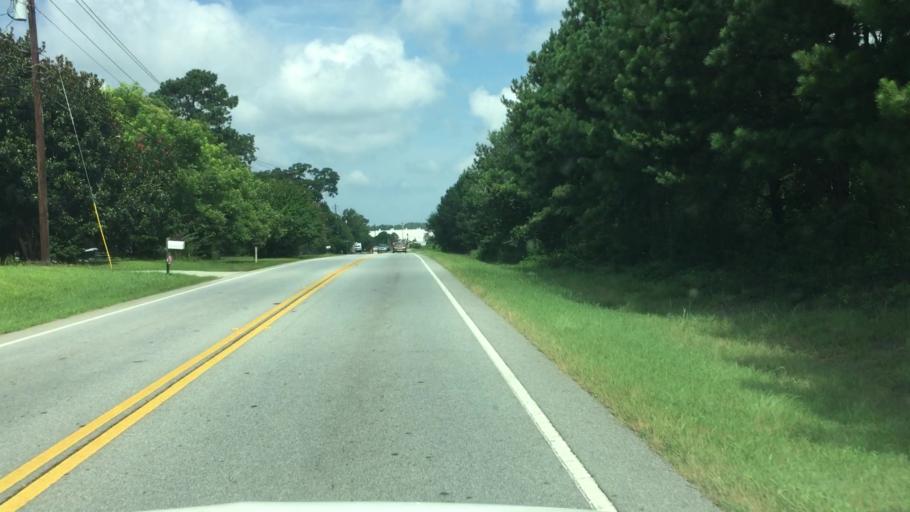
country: US
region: Georgia
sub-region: Barrow County
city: Auburn
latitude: 33.9995
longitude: -83.7949
